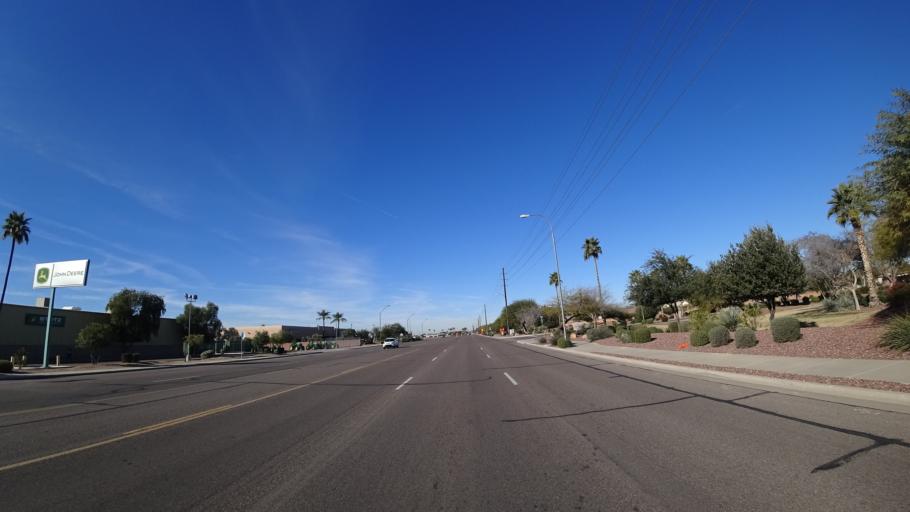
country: US
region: Arizona
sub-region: Maricopa County
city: Tolleson
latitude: 33.4643
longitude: -112.2991
